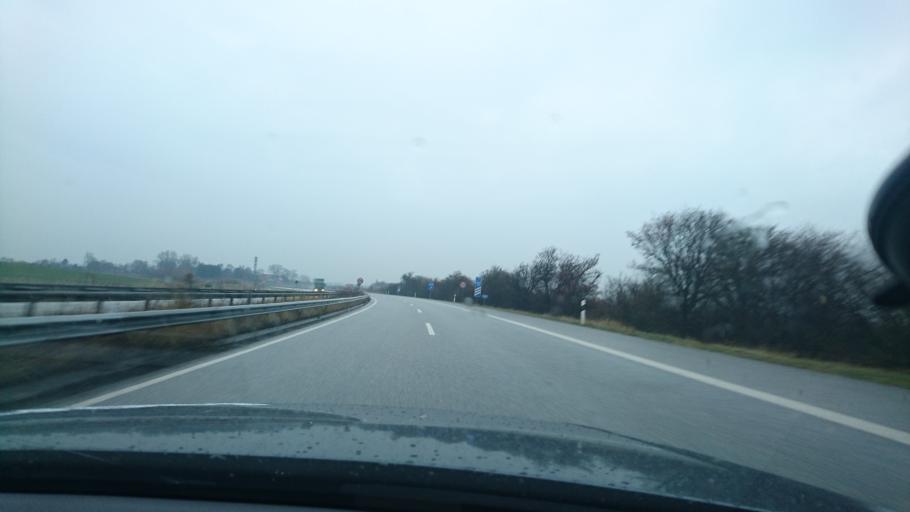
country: DE
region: Schleswig-Holstein
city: Gremersdorf
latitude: 54.3250
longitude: 10.9312
